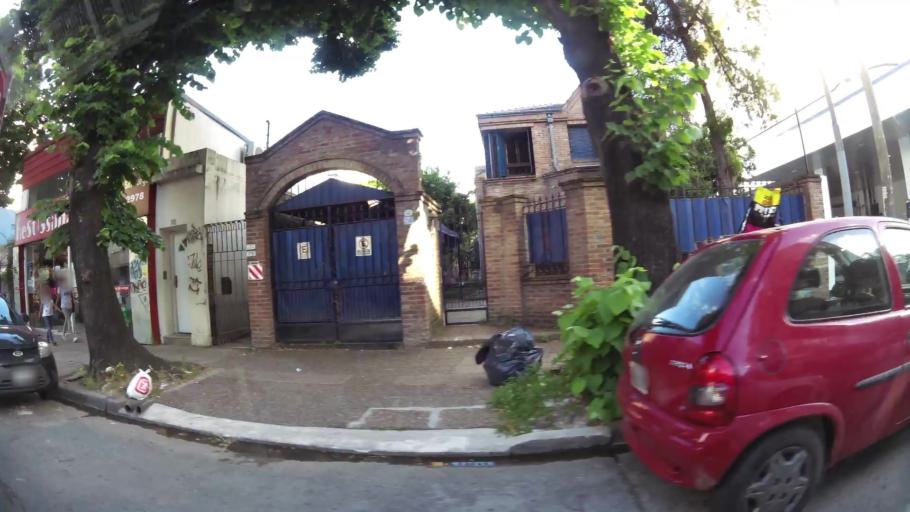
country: AR
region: Buenos Aires
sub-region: Partido de General San Martin
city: General San Martin
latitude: -34.5496
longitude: -58.5515
